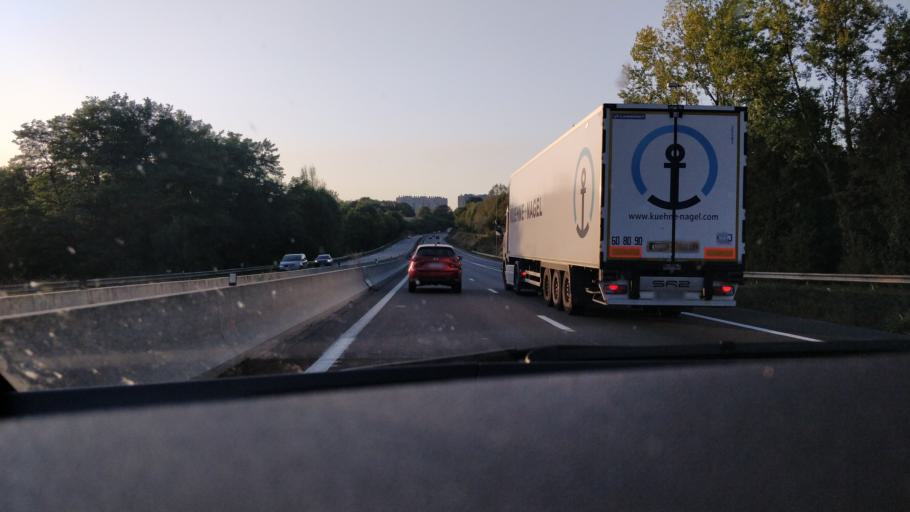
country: FR
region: Limousin
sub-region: Departement de la Haute-Vienne
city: Condat-sur-Vienne
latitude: 45.8199
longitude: 1.2913
